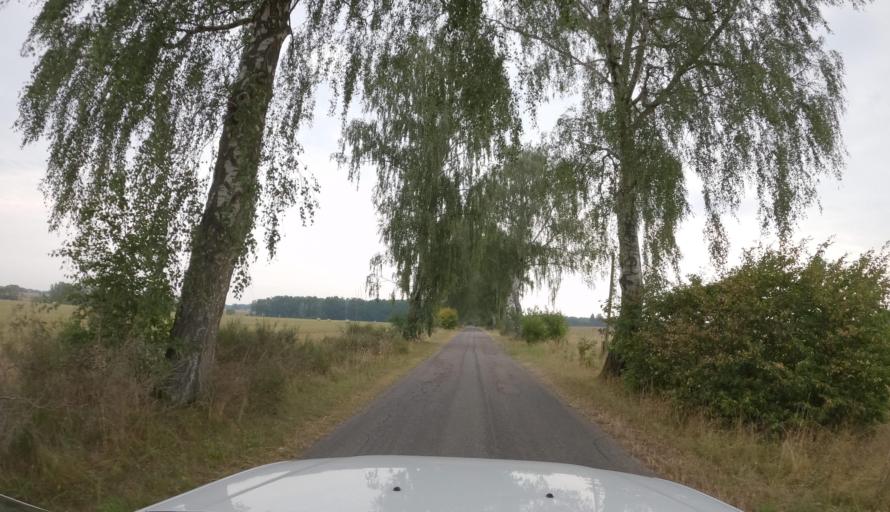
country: PL
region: West Pomeranian Voivodeship
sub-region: Powiat kolobrzeski
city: Ryman
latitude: 53.8314
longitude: 15.5863
